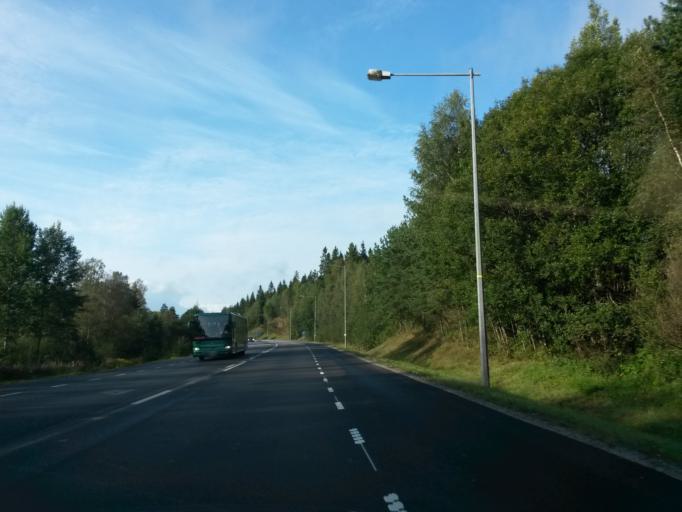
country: SE
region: Vaestra Goetaland
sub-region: Boras Kommun
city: Boras
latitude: 57.6920
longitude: 12.9450
